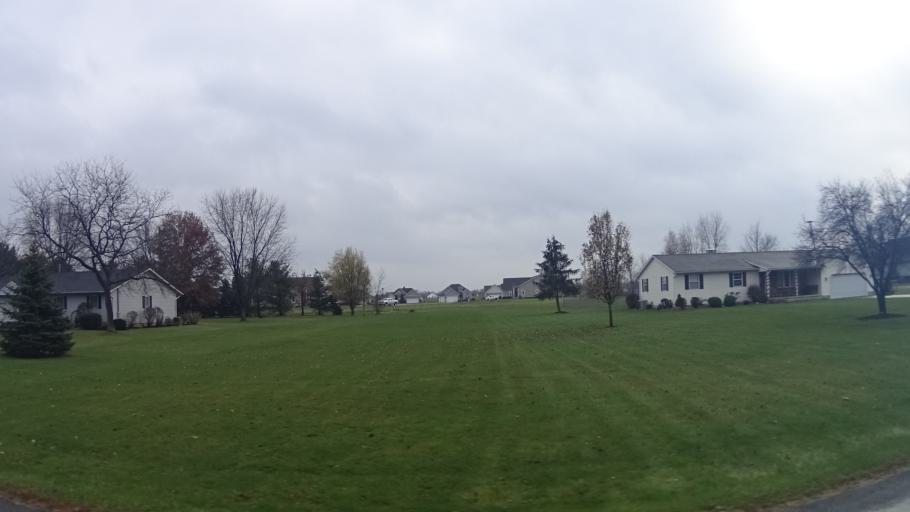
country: US
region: Ohio
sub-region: Lorain County
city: Lagrange
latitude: 41.2524
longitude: -82.1144
